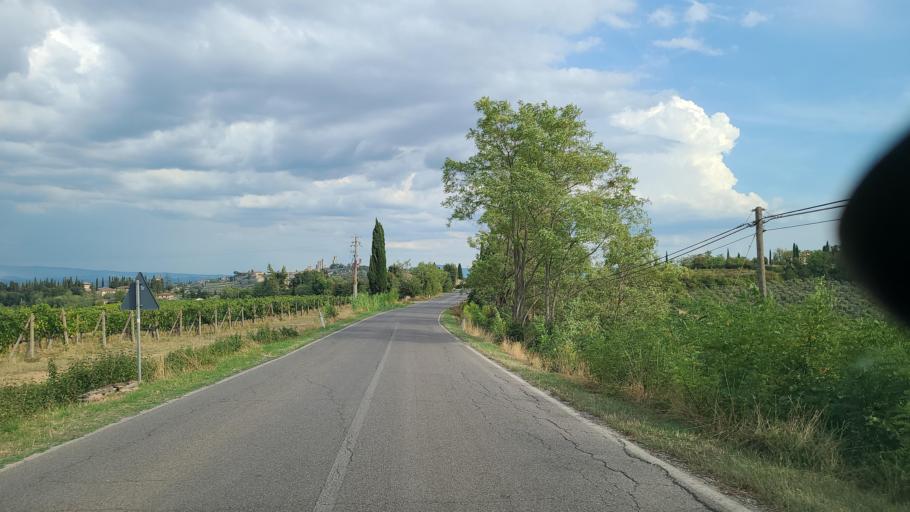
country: IT
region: Tuscany
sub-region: Provincia di Siena
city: San Gimignano
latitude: 43.4801
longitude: 11.0161
